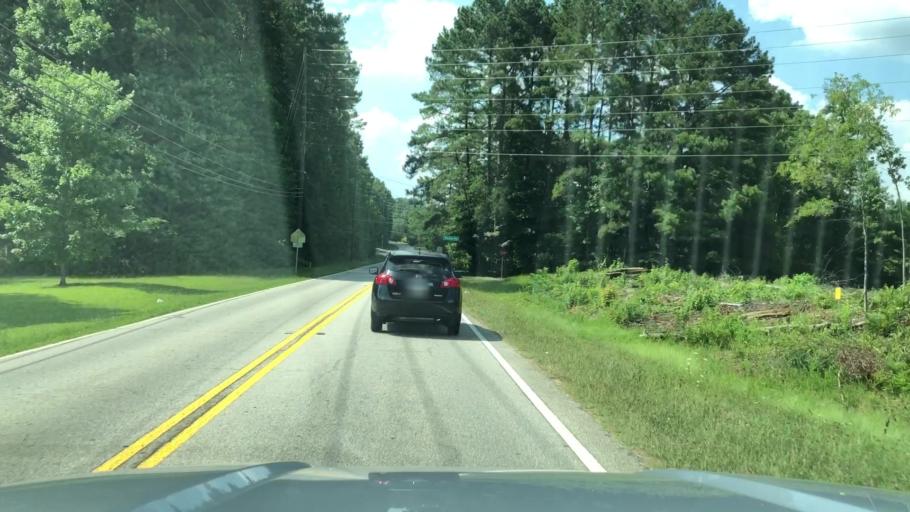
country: US
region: Georgia
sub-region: Paulding County
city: Dallas
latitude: 33.9624
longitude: -84.7905
